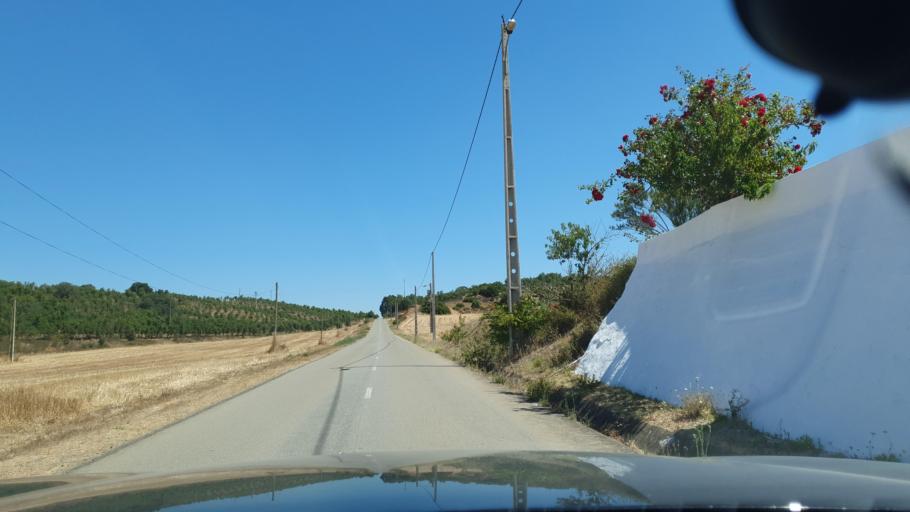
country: PT
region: Beja
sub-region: Odemira
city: Odemira
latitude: 37.5434
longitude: -8.4610
